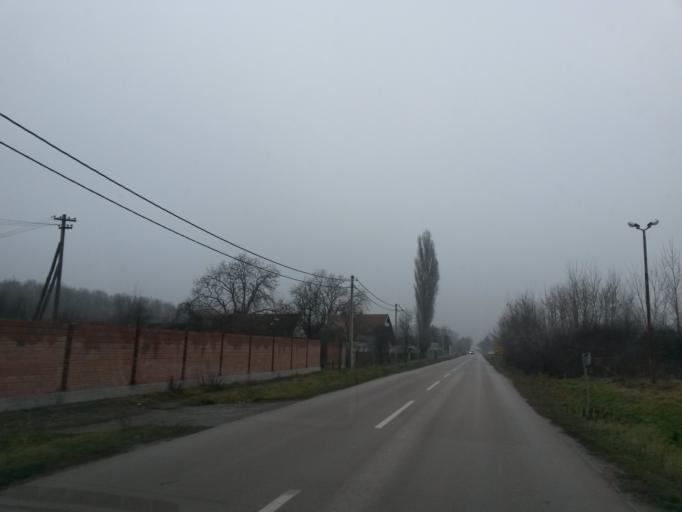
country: HR
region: Vukovarsko-Srijemska
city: Cerna
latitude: 45.2007
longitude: 18.7018
